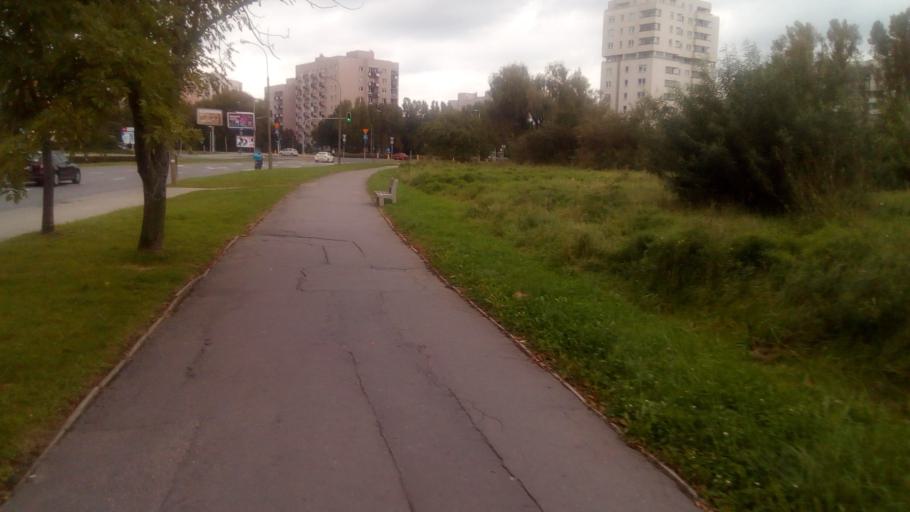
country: PL
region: Masovian Voivodeship
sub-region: Warszawa
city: Ursynow
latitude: 52.1538
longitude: 21.0495
